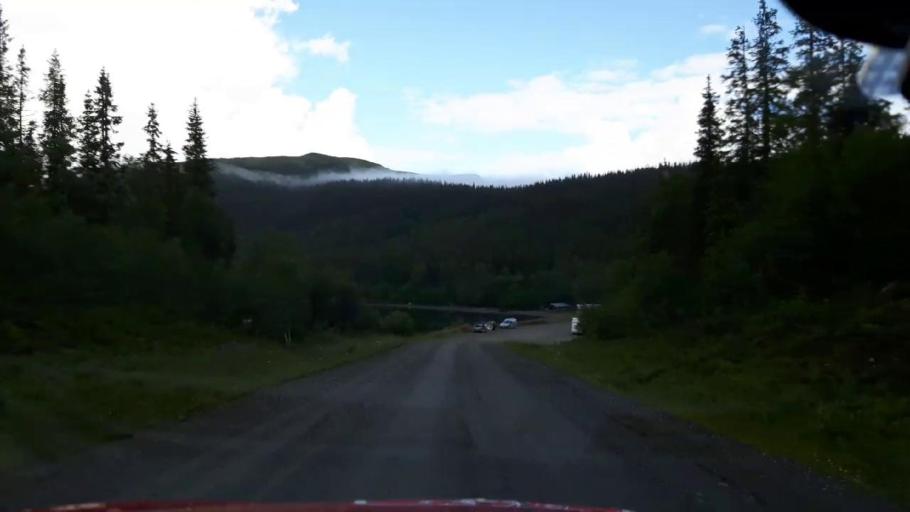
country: NO
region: Nordland
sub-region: Hattfjelldal
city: Hattfjelldal
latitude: 64.8856
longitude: 14.7646
